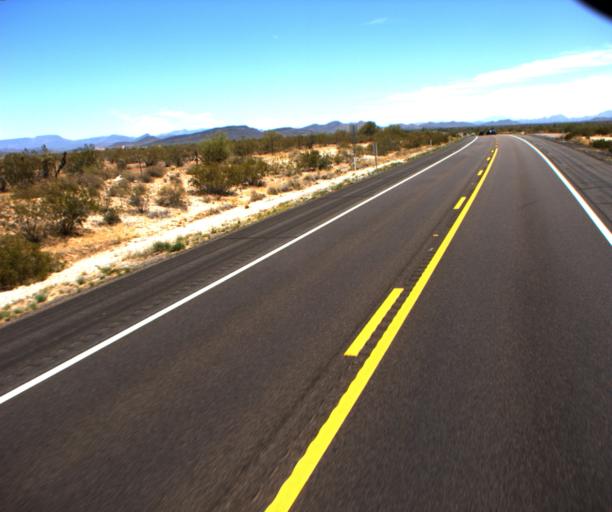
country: US
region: Arizona
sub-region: Maricopa County
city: Anthem
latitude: 33.7980
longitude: -112.2275
